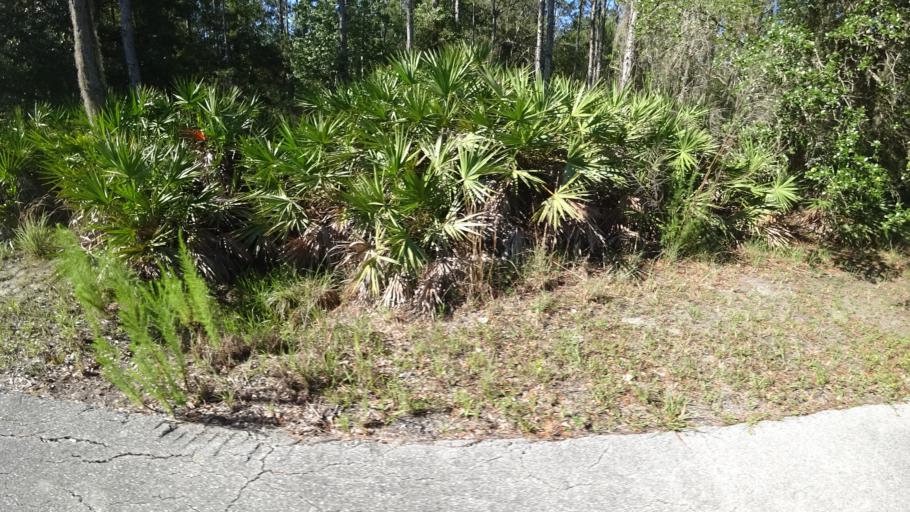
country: US
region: Florida
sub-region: Sarasota County
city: The Meadows
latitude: 27.4092
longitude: -82.3104
